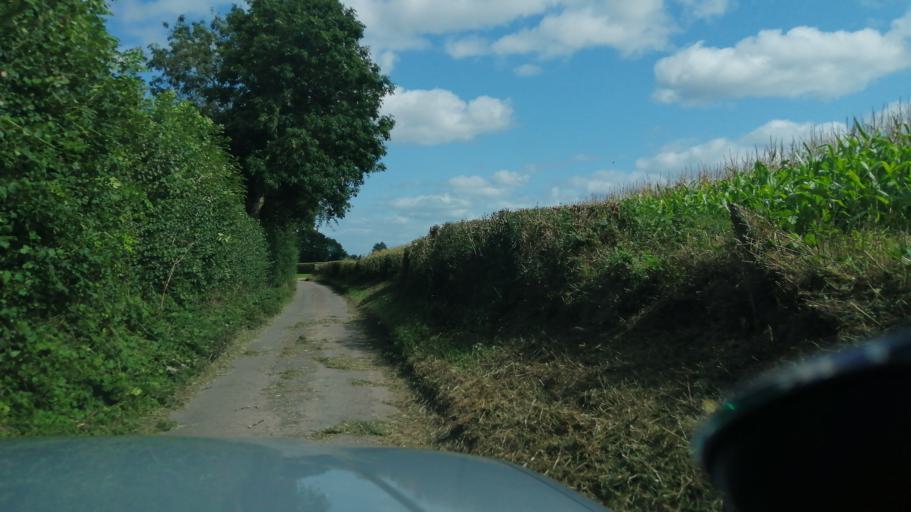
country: GB
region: England
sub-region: Herefordshire
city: Thruxton
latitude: 52.0115
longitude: -2.8074
